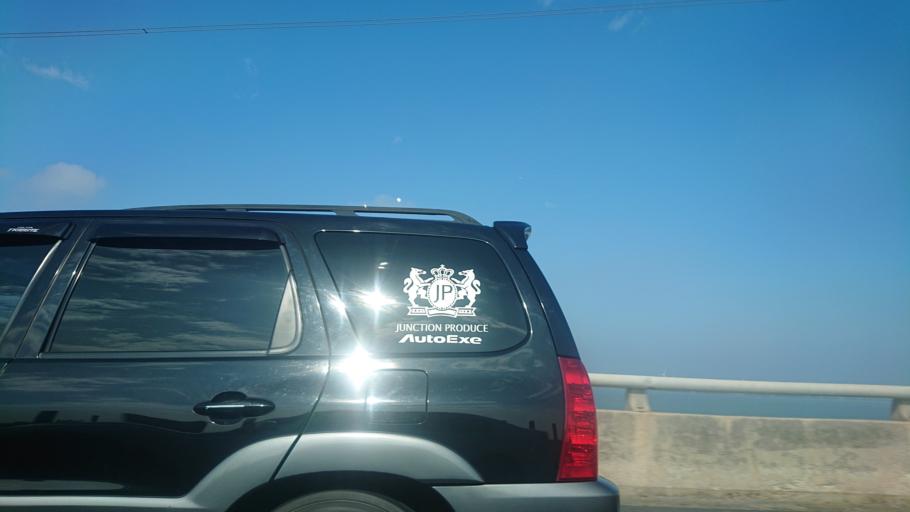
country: TW
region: Taiwan
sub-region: Changhua
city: Chang-hua
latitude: 24.0844
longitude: 120.4233
